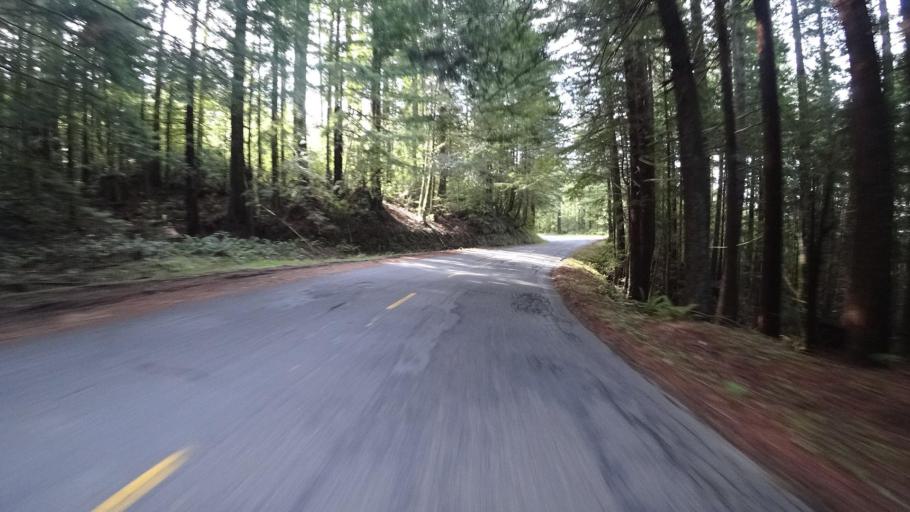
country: US
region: California
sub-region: Humboldt County
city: Bayside
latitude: 40.7613
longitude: -124.0006
